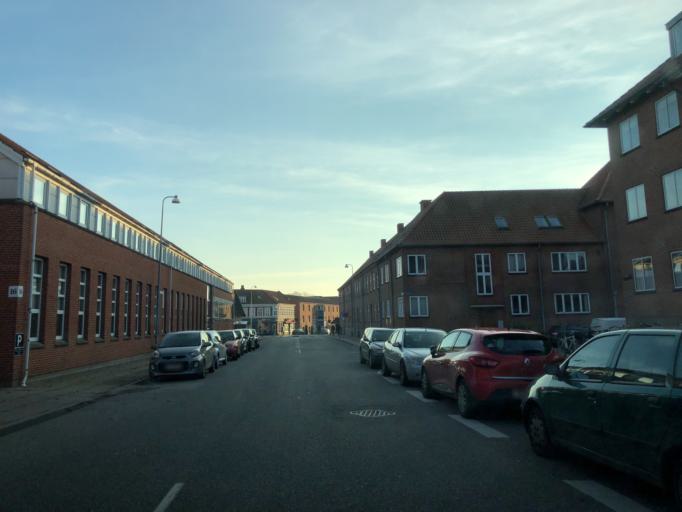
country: DK
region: South Denmark
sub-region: Fredericia Kommune
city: Fredericia
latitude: 55.5713
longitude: 9.7500
